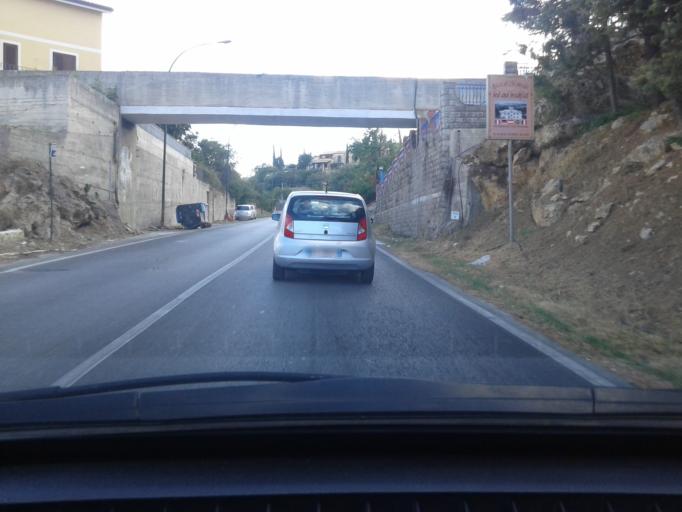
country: IT
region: Sicily
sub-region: Palermo
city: Monreale
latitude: 38.0833
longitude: 13.3004
